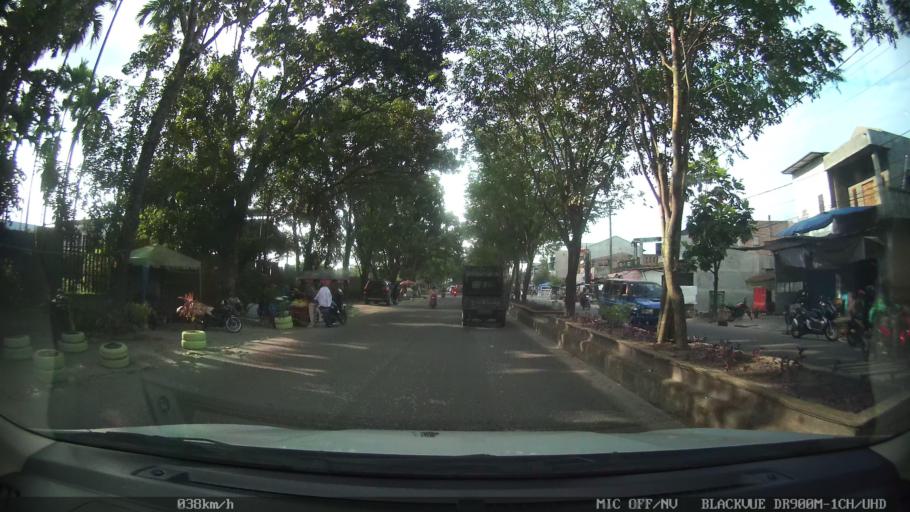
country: ID
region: North Sumatra
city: Sunggal
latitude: 3.5615
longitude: 98.6165
